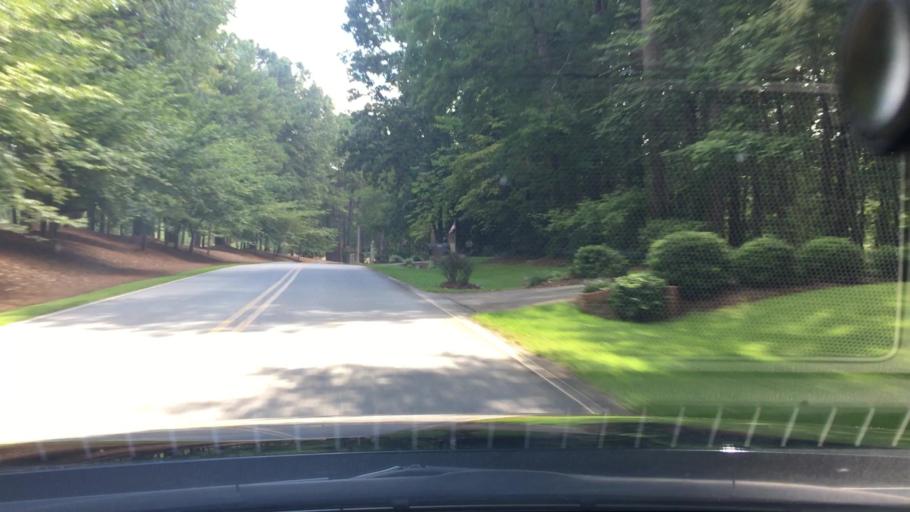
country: US
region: Georgia
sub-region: Putnam County
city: Jefferson
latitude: 33.3910
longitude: -83.2416
